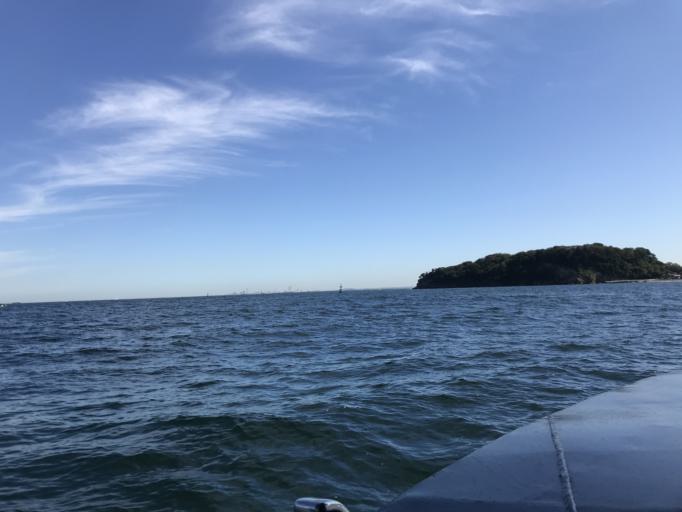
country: JP
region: Kanagawa
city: Yokosuka
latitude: 35.2862
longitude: 139.6845
